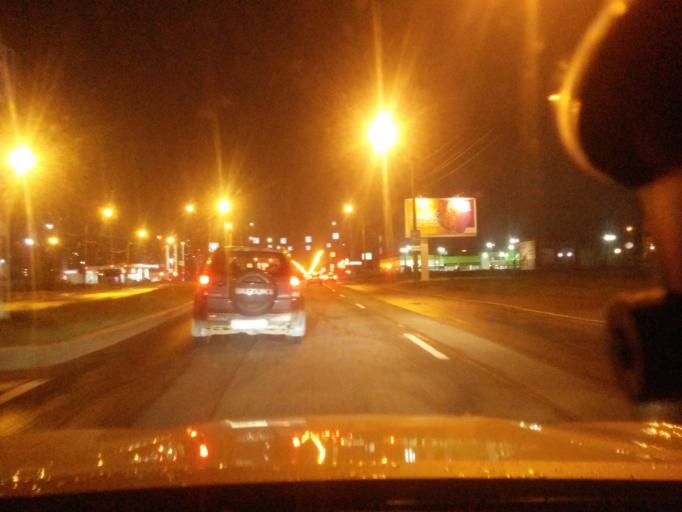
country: RU
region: Leningrad
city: Parnas
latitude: 60.0643
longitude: 30.3439
